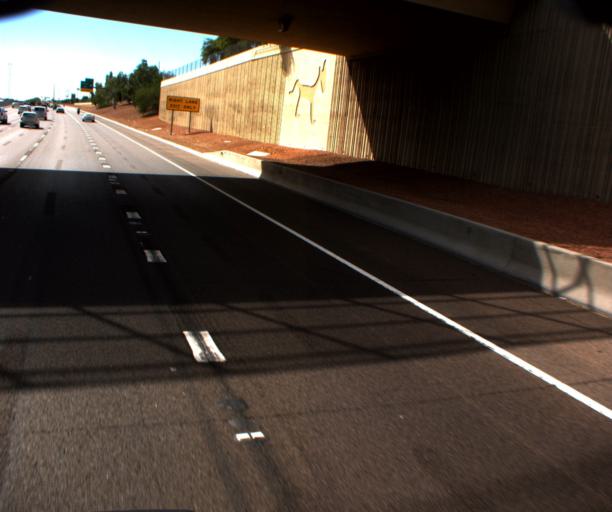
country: US
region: Arizona
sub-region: Maricopa County
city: San Carlos
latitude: 33.3566
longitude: -111.8946
